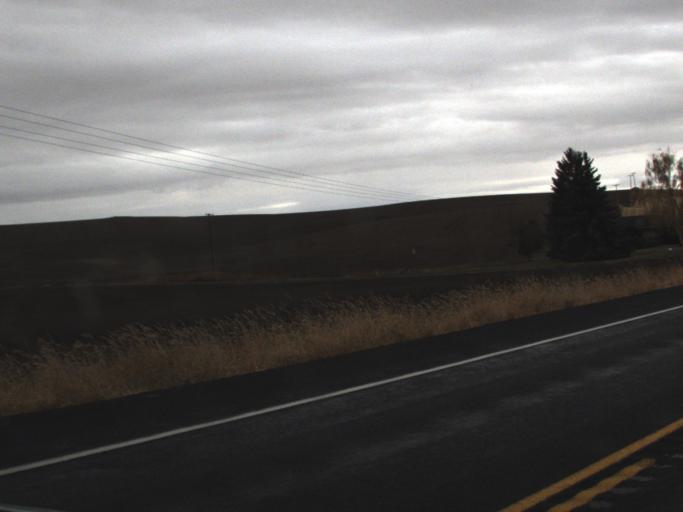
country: US
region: Washington
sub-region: Whitman County
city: Pullman
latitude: 46.6748
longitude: -117.1951
